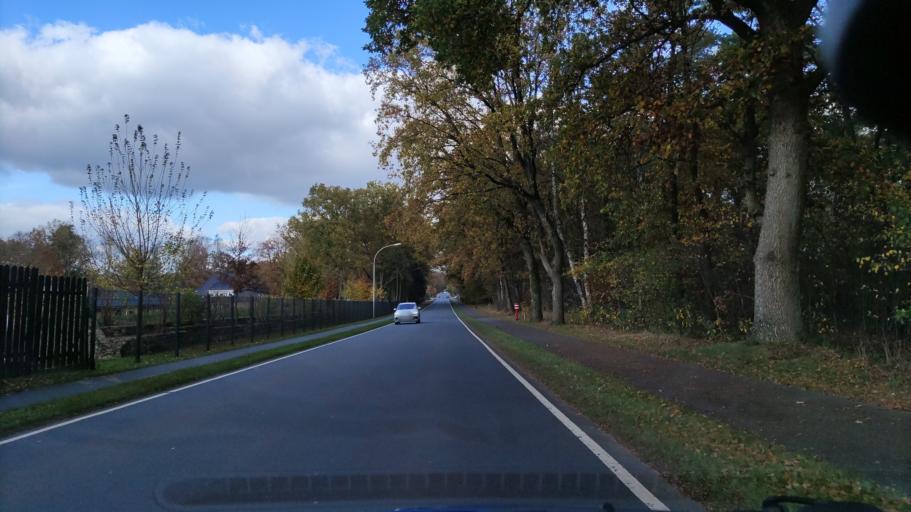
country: DE
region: Lower Saxony
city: Munster
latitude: 53.0073
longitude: 10.0880
